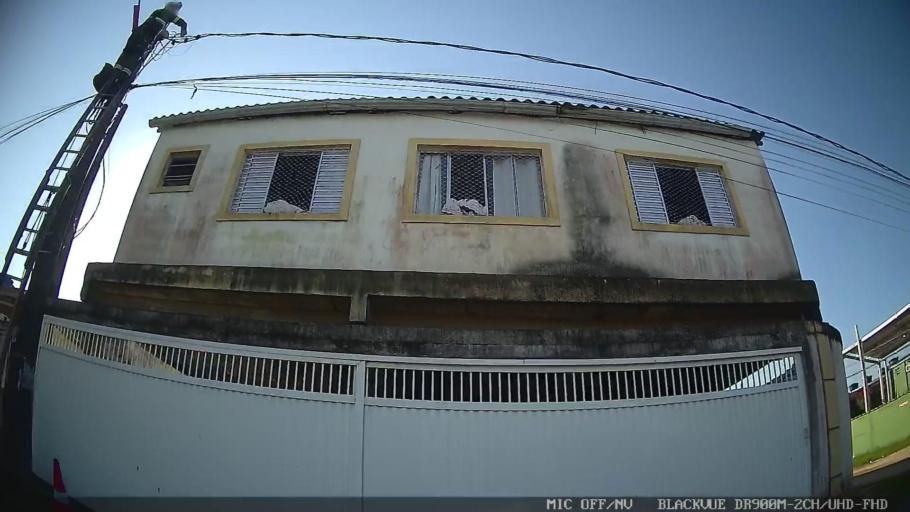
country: BR
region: Sao Paulo
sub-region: Guaruja
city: Guaruja
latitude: -23.9733
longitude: -46.2243
